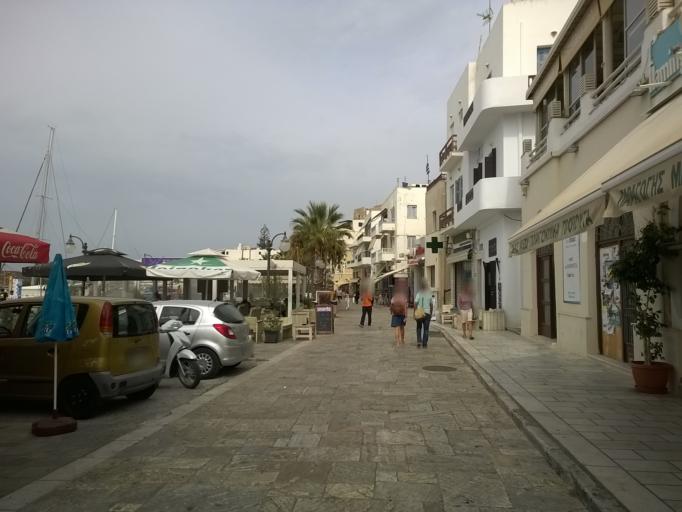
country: GR
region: South Aegean
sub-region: Nomos Kykladon
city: Naxos
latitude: 37.1043
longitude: 25.3753
